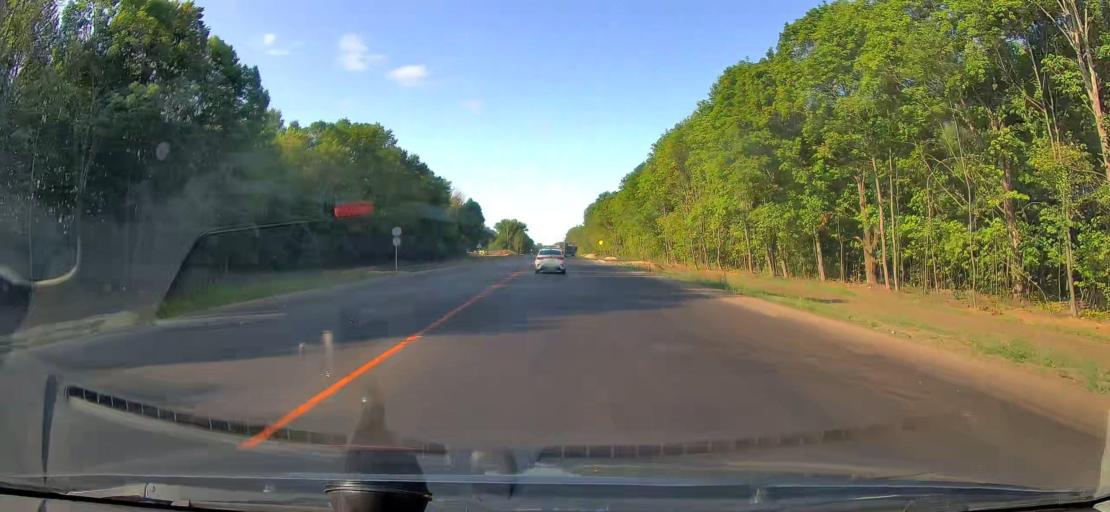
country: RU
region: Orjol
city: Spasskoye-Lutovinovo
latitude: 53.3578
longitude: 36.7212
